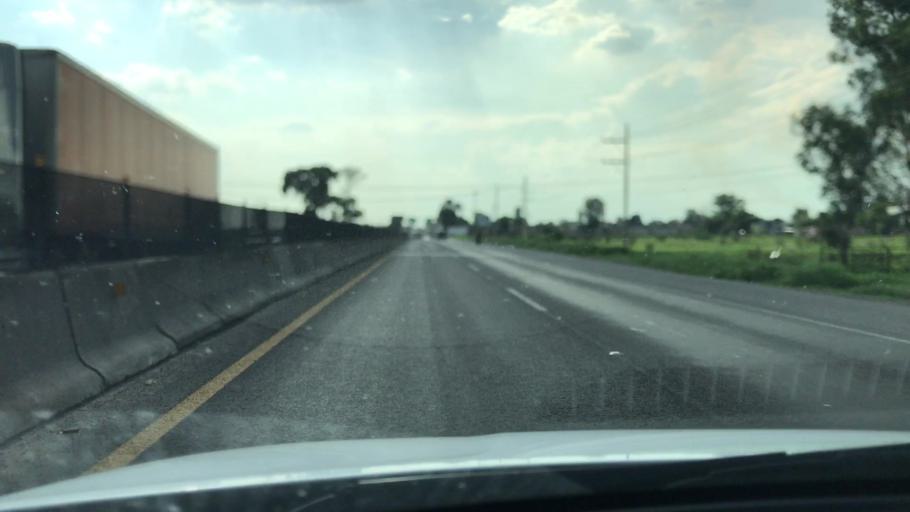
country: MX
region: Guanajuato
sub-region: Salamanca
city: El Divisador
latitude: 20.5568
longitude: -101.1609
